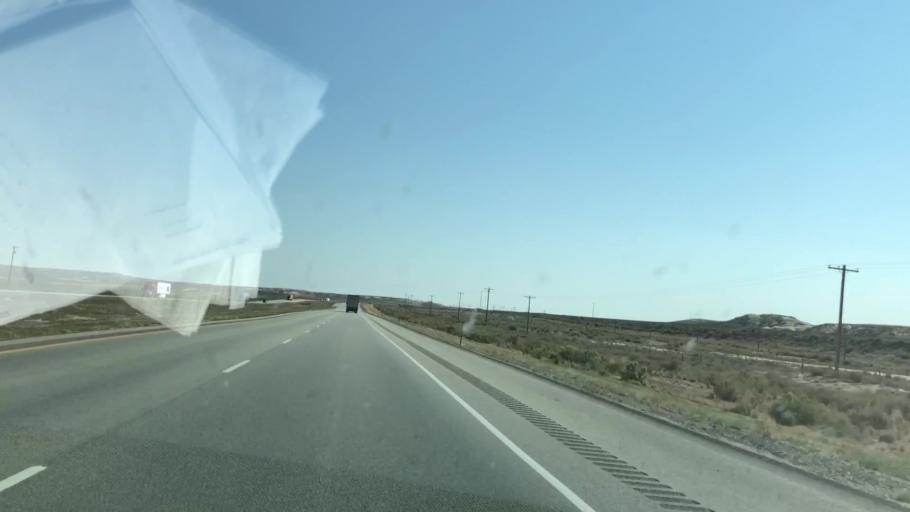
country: US
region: Wyoming
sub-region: Carbon County
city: Rawlins
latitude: 41.6996
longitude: -107.9092
